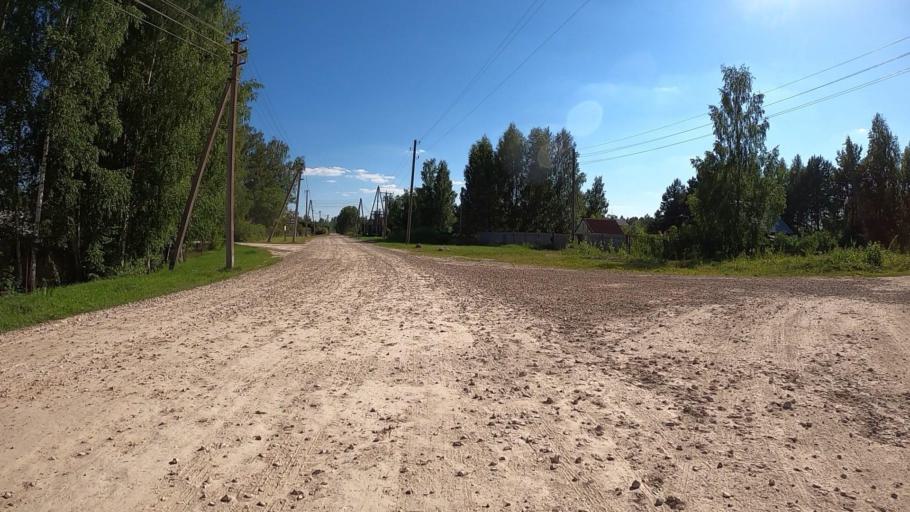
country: LV
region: Stopini
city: Ulbroka
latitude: 56.8862
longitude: 24.2919
